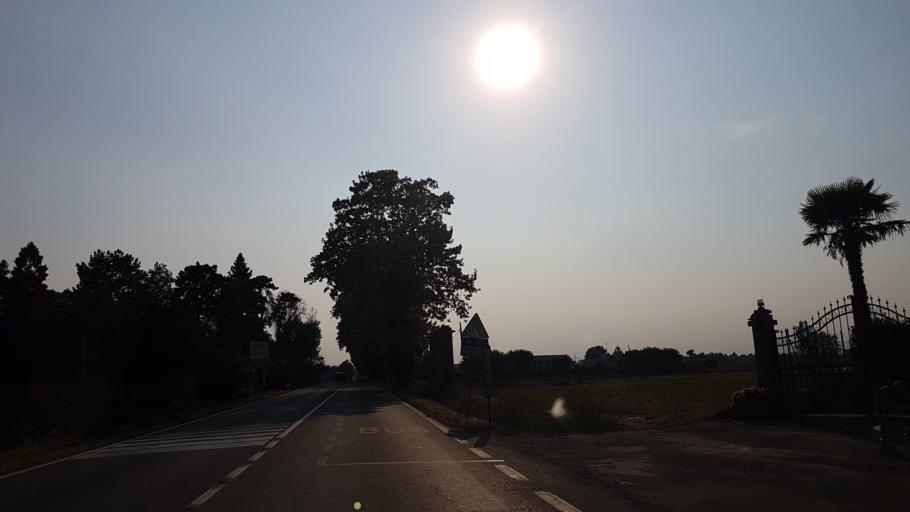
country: IT
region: Emilia-Romagna
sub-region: Provincia di Parma
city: Vicofertile
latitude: 44.7757
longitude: 10.2742
